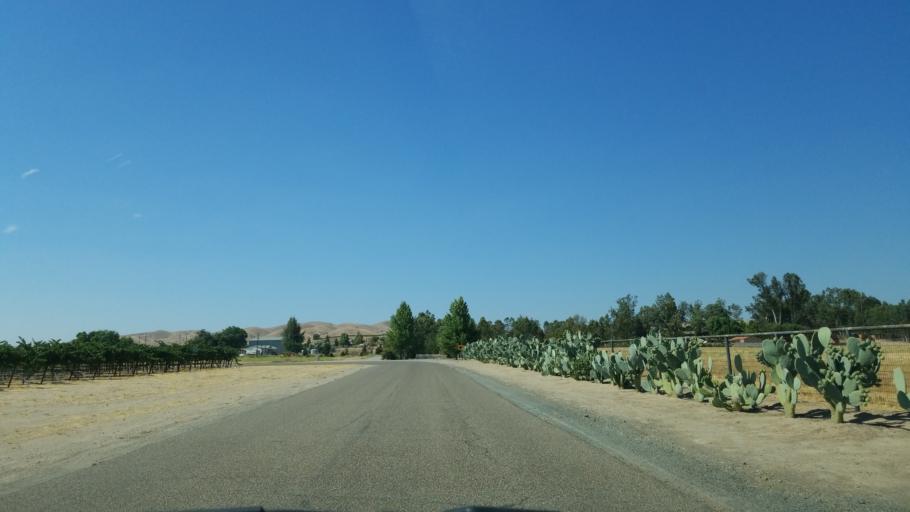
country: US
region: California
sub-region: San Luis Obispo County
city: San Miguel
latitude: 35.7206
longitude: -120.6495
